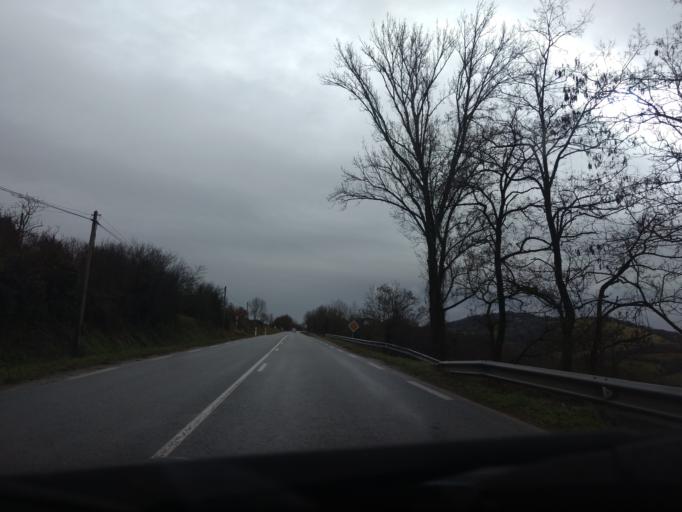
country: FR
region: Midi-Pyrenees
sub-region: Departement de l'Aveyron
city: Saint-Christophe-Vallon
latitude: 44.5079
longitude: 2.3630
